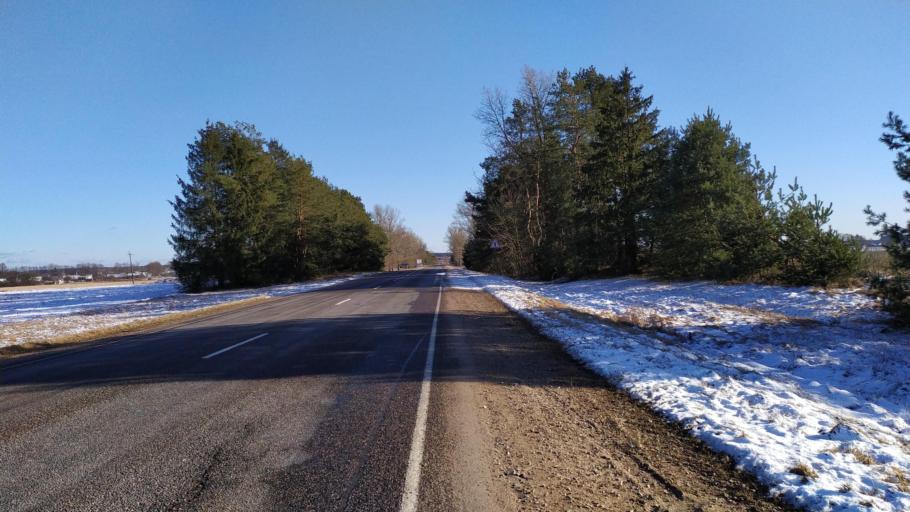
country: BY
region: Brest
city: Kamyanyets
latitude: 52.3755
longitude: 23.8752
